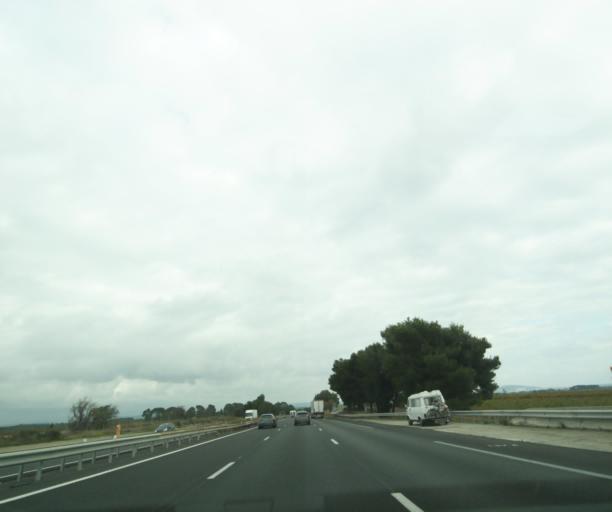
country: FR
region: Languedoc-Roussillon
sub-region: Departement de l'Herault
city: Pinet
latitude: 43.4202
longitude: 3.5332
